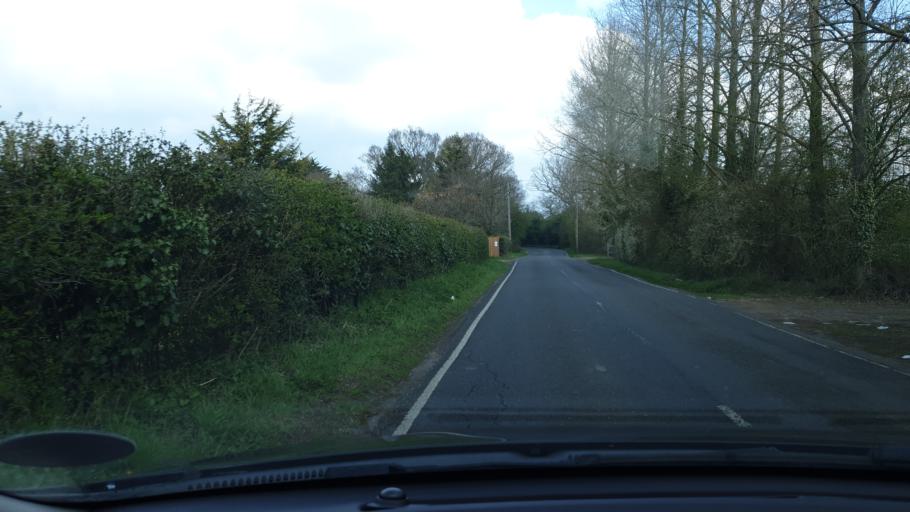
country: GB
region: England
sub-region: Essex
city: Great Bentley
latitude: 51.8620
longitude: 1.1000
